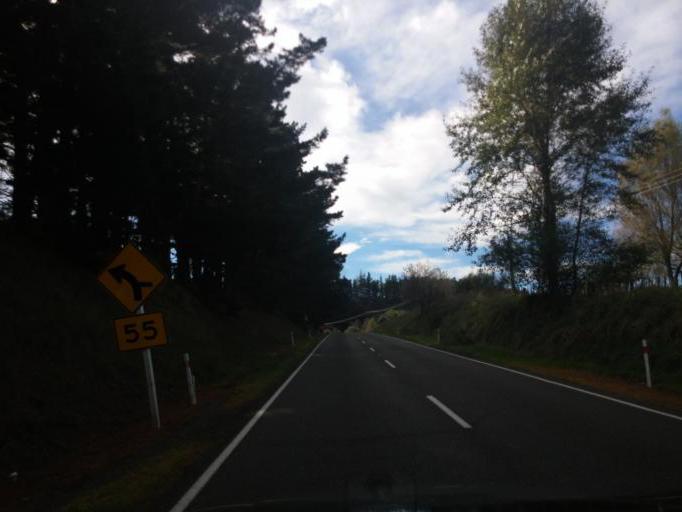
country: NZ
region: Manawatu-Wanganui
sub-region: Palmerston North City
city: Palmerston North
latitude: -40.3928
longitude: 175.6348
